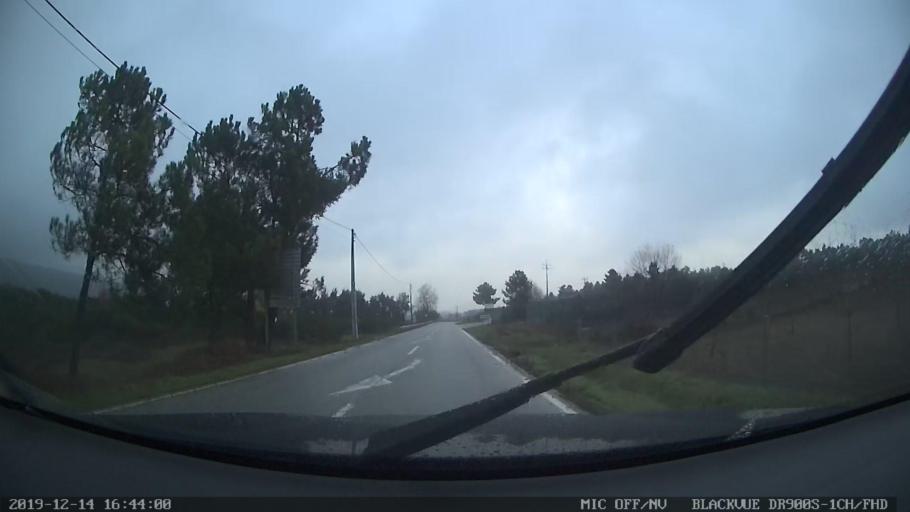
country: PT
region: Vila Real
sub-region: Murca
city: Murca
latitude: 41.3874
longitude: -7.4975
